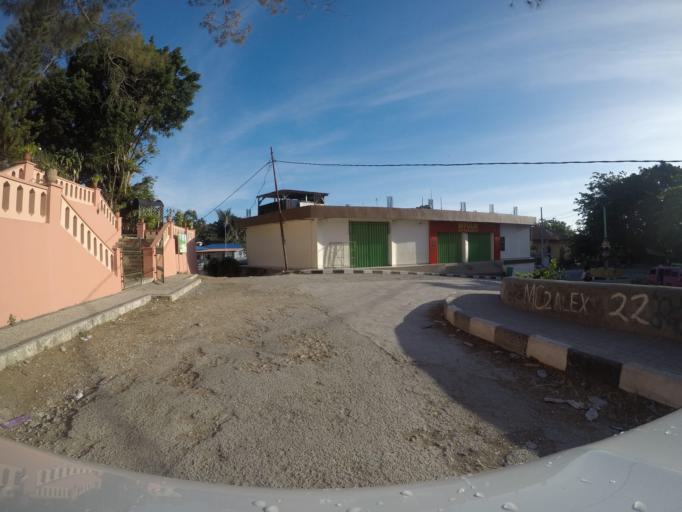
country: TL
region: Baucau
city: Baucau
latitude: -8.4638
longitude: 126.4533
